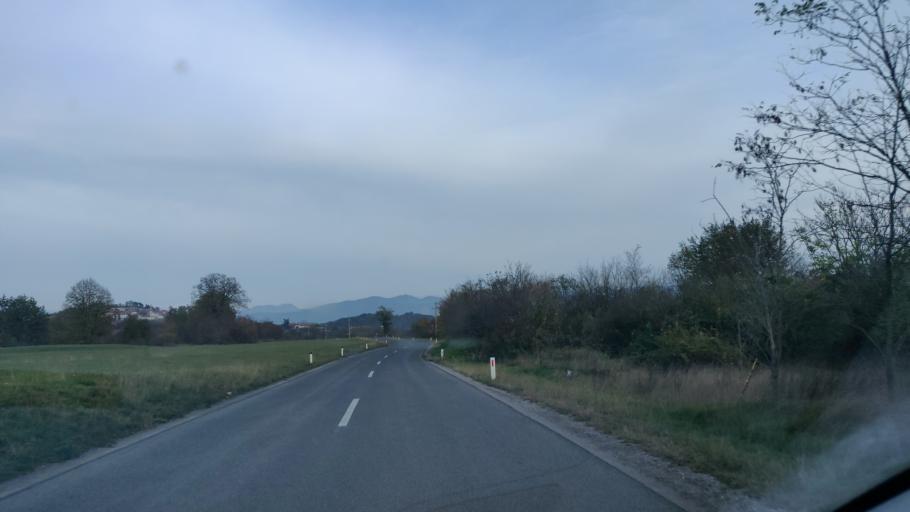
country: SI
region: Komen
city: Komen
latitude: 45.8172
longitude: 13.8287
